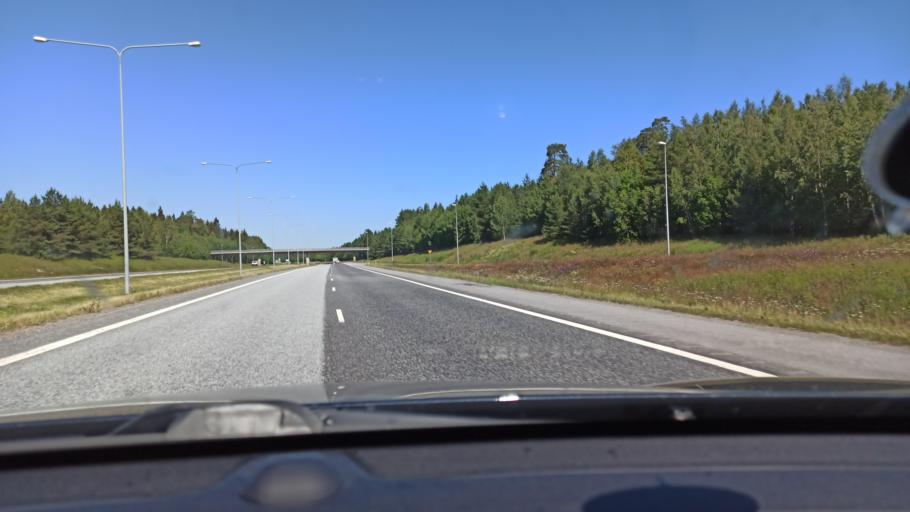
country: FI
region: Ostrobothnia
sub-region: Vaasa
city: Ristinummi
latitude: 63.0552
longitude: 21.7133
